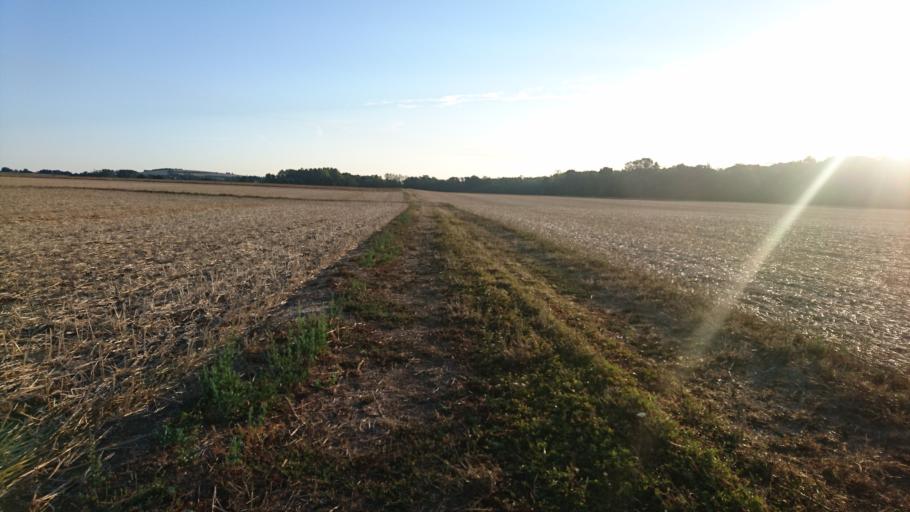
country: FR
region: Bourgogne
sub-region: Departement de l'Yonne
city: Fleury-la-Vallee
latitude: 47.8730
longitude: 3.4020
